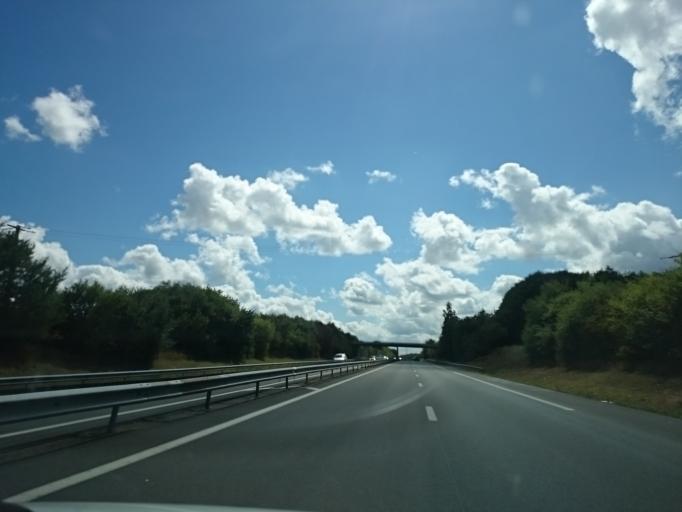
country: FR
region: Pays de la Loire
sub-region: Departement de Maine-et-Loire
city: Durtal
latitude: 47.7345
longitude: -0.2481
